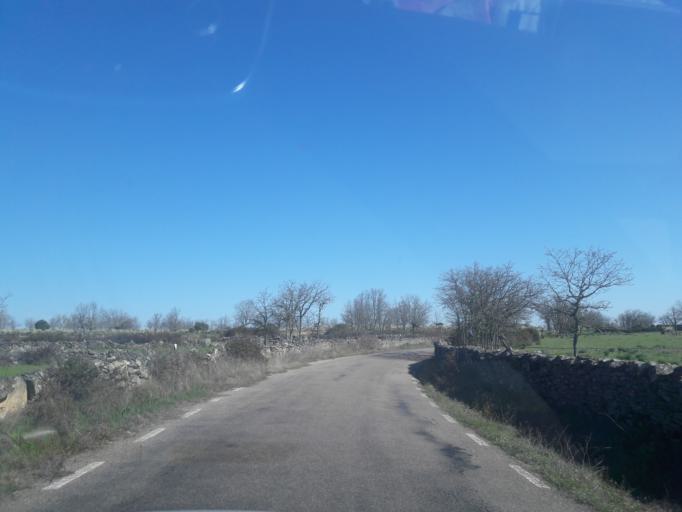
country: ES
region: Castille and Leon
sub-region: Provincia de Salamanca
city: Valsalabroso
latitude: 41.1186
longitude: -6.4834
